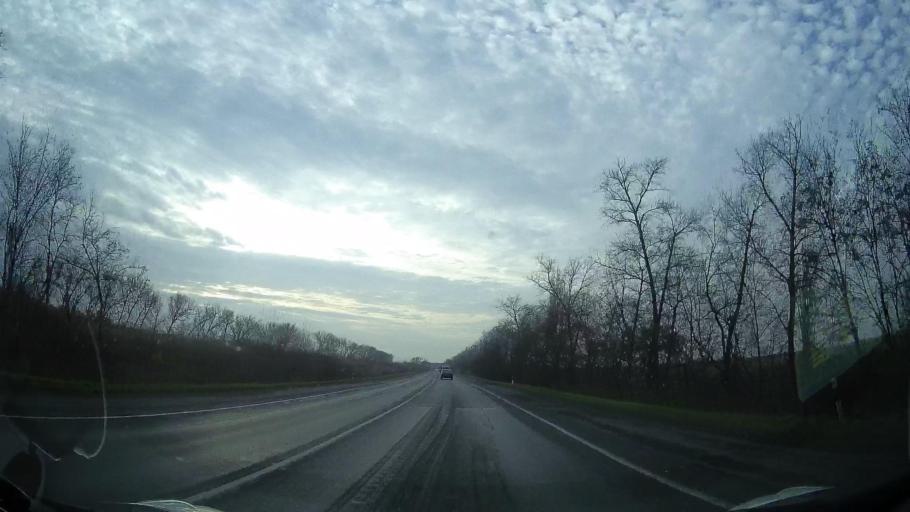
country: RU
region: Rostov
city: Starocherkasskaya
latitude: 47.1598
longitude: 40.2231
